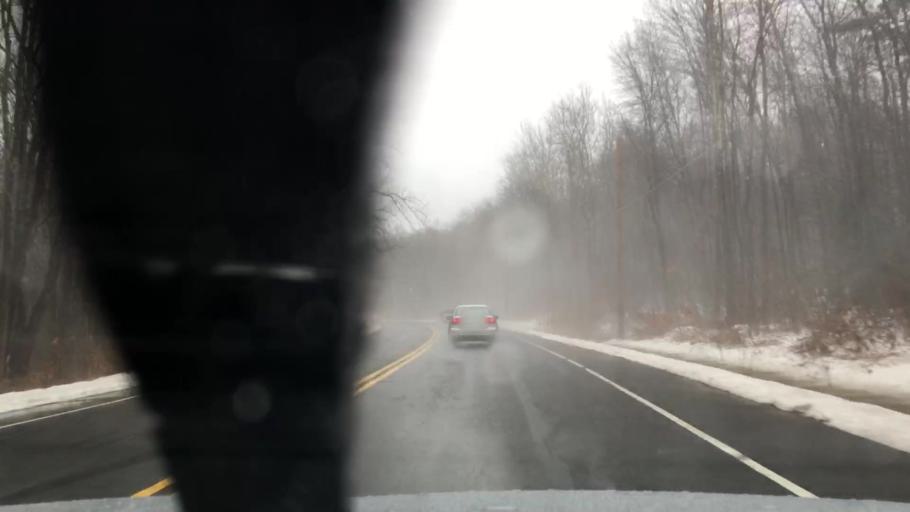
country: US
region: Massachusetts
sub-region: Hampden County
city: Ludlow
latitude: 42.2038
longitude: -72.4929
